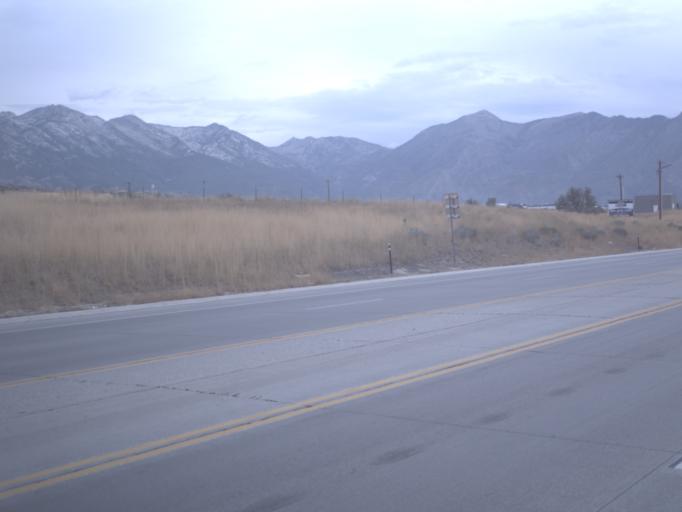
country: US
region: Utah
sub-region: Utah County
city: Lehi
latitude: 40.4328
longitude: -111.8517
